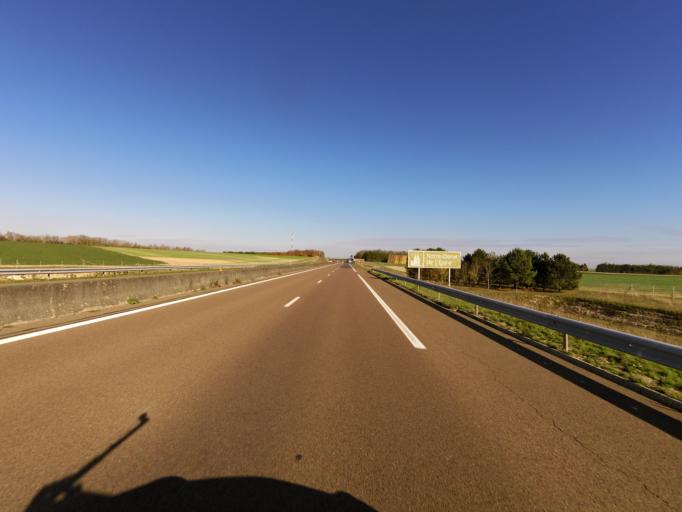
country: FR
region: Champagne-Ardenne
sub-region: Departement de la Marne
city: Compertrix
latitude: 48.8738
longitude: 4.2891
